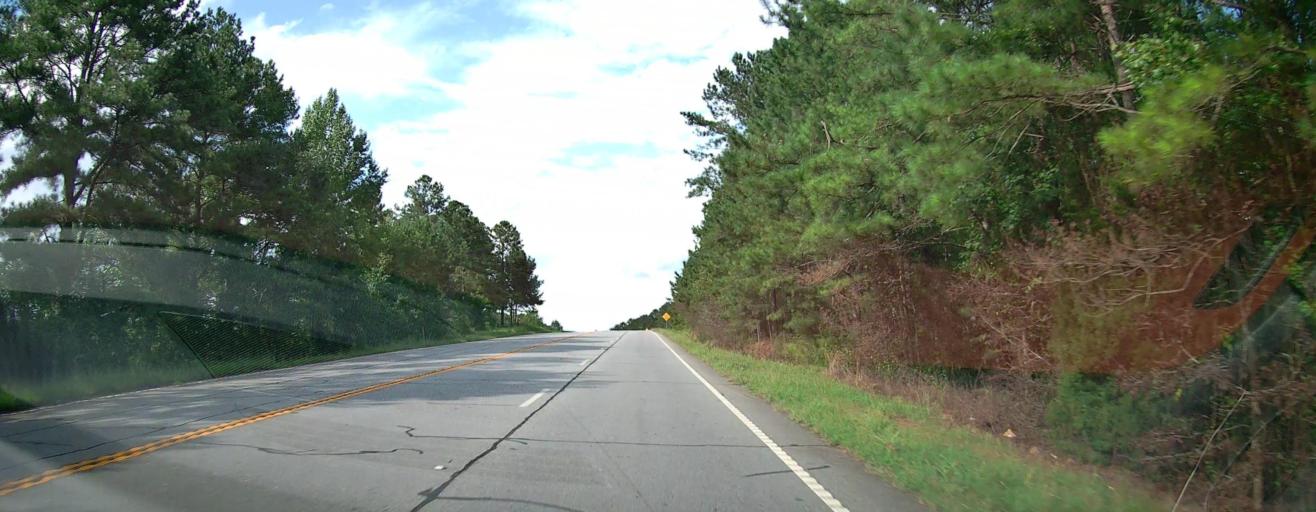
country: US
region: Georgia
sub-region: Meriwether County
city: Greenville
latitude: 33.0058
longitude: -84.5680
